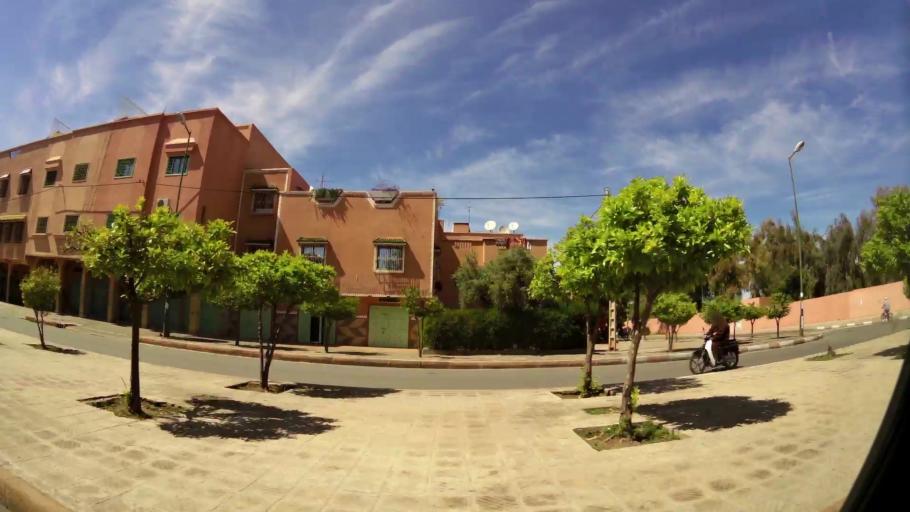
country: MA
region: Marrakech-Tensift-Al Haouz
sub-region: Marrakech
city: Marrakesh
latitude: 31.6056
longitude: -7.9701
